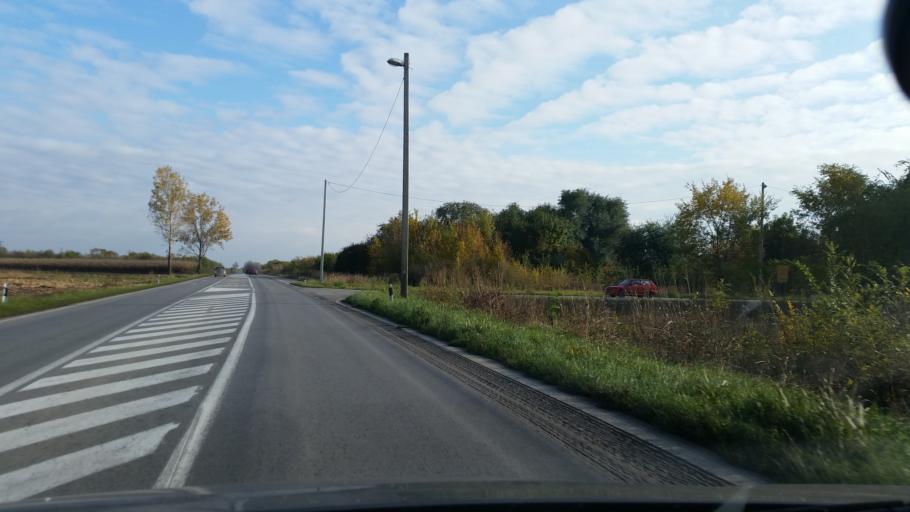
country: RS
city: Ecka
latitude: 45.3316
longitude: 20.4383
